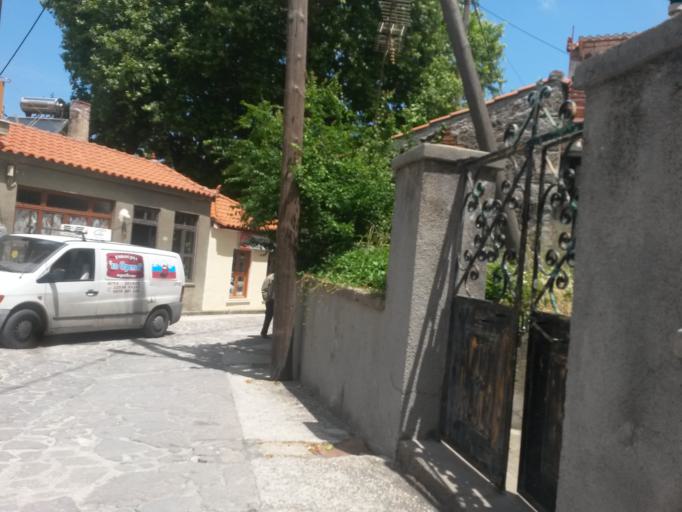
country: GR
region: North Aegean
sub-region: Nomos Lesvou
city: Petra
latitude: 39.2599
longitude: 26.0744
